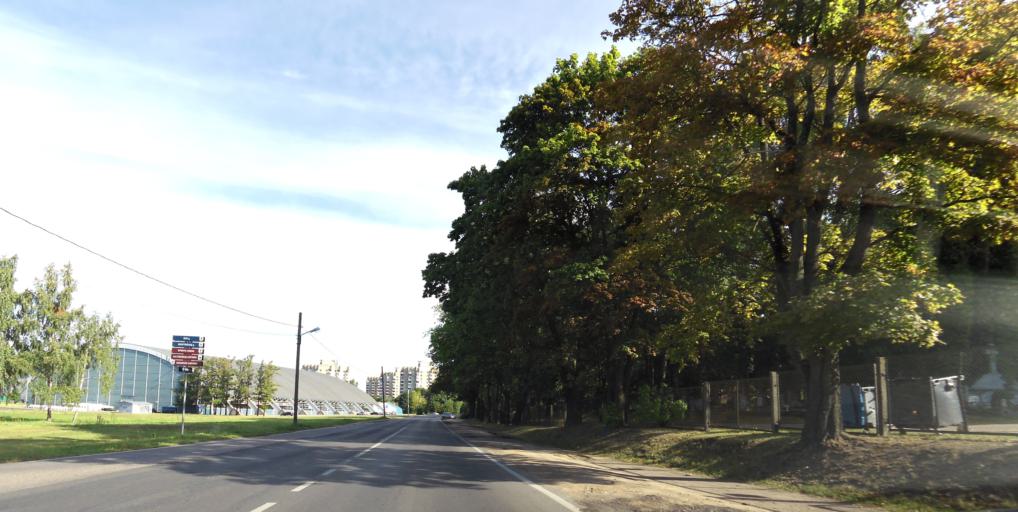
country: LT
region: Vilnius County
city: Seskine
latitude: 54.7058
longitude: 25.2378
